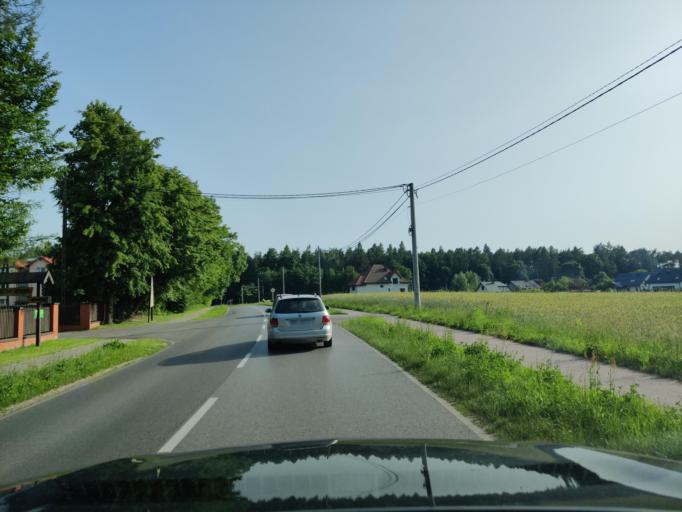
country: PL
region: Masovian Voivodeship
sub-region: Powiat wyszkowski
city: Wyszkow
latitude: 52.6362
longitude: 21.4517
